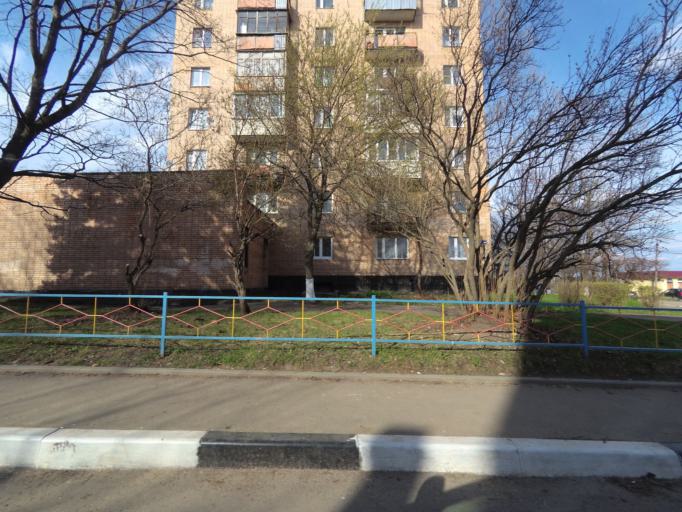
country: RU
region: Moskovskaya
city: Lugovaya
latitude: 56.0457
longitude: 37.4838
